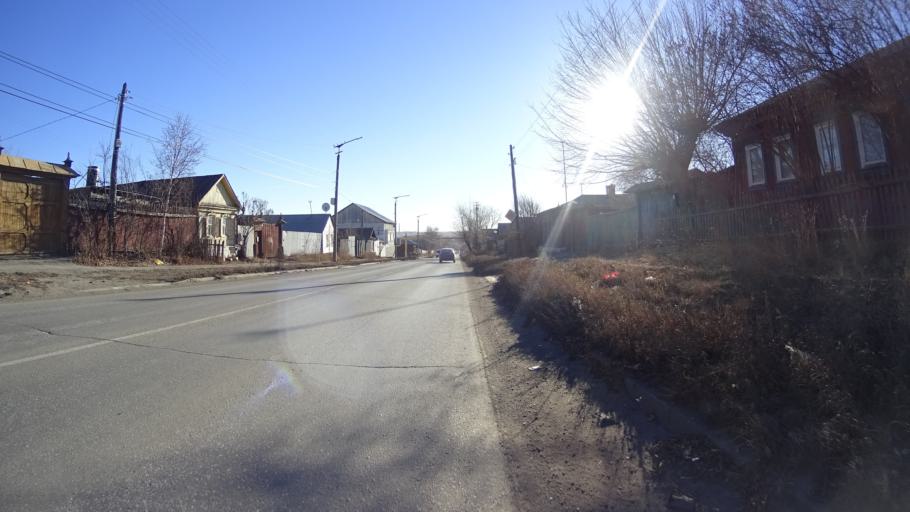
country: RU
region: Chelyabinsk
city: Troitsk
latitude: 54.1010
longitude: 61.5624
